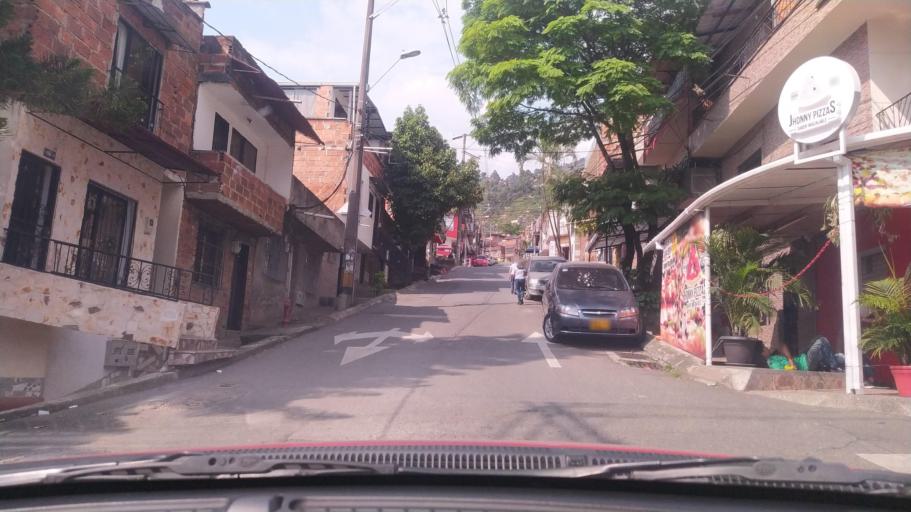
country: CO
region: Antioquia
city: Medellin
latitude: 6.2685
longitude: -75.5478
